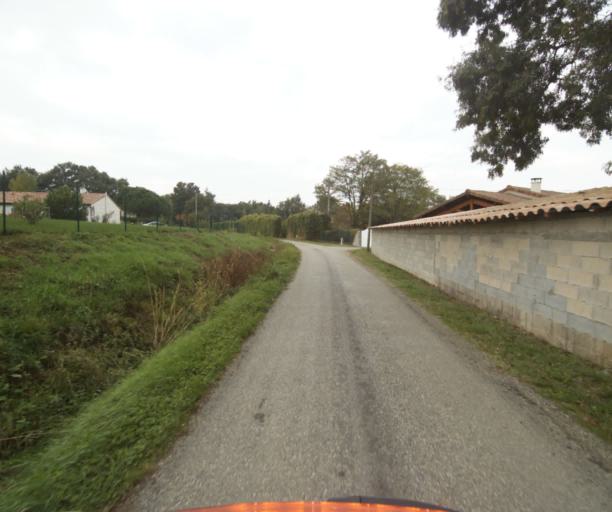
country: FR
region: Midi-Pyrenees
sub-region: Departement du Tarn-et-Garonne
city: Verdun-sur-Garonne
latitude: 43.8229
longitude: 1.2111
